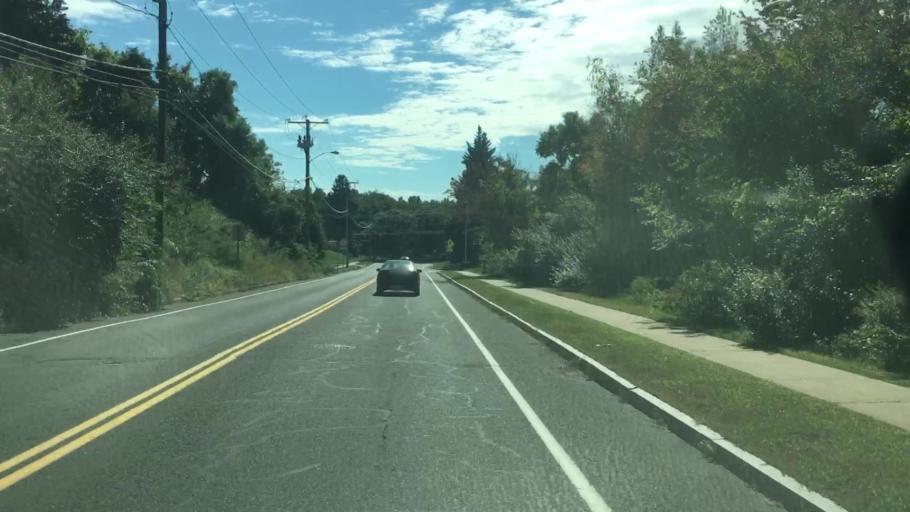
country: US
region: Connecticut
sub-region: Hartford County
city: Manchester
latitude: 41.8048
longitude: -72.5343
